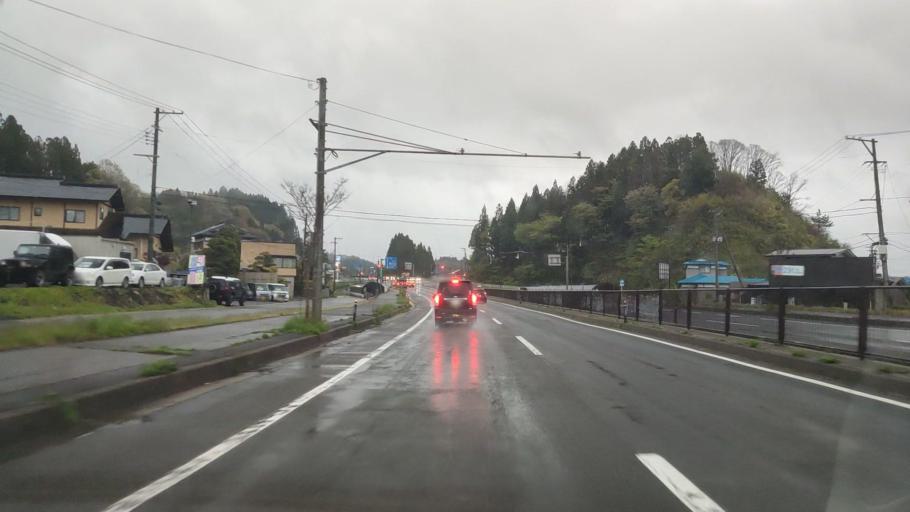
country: JP
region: Akita
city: Akita
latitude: 39.6549
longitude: 140.2075
